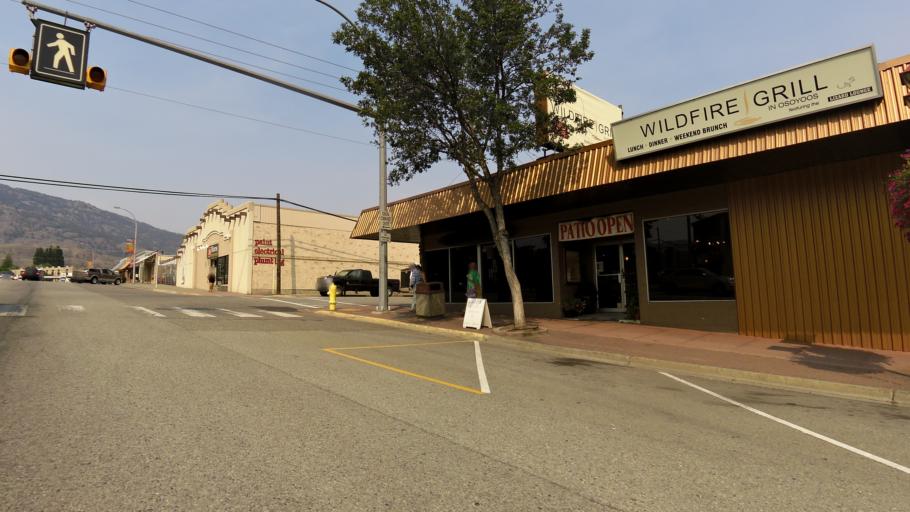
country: CA
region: British Columbia
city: Osoyoos
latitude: 49.0329
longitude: -119.4669
